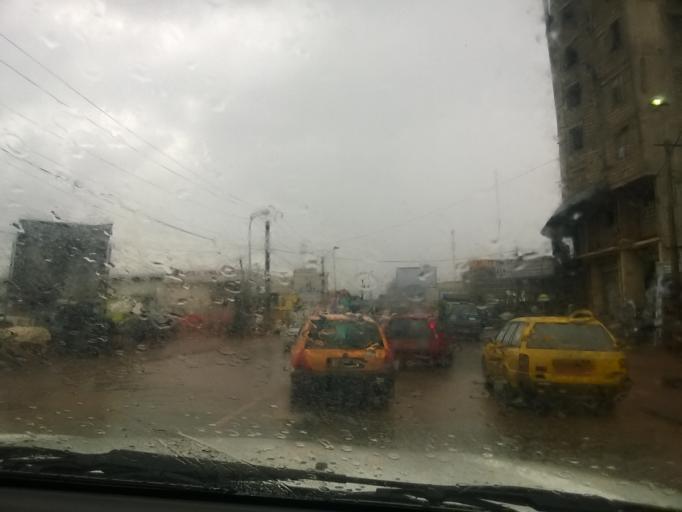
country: CM
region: Centre
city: Yaounde
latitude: 3.8686
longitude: 11.5329
